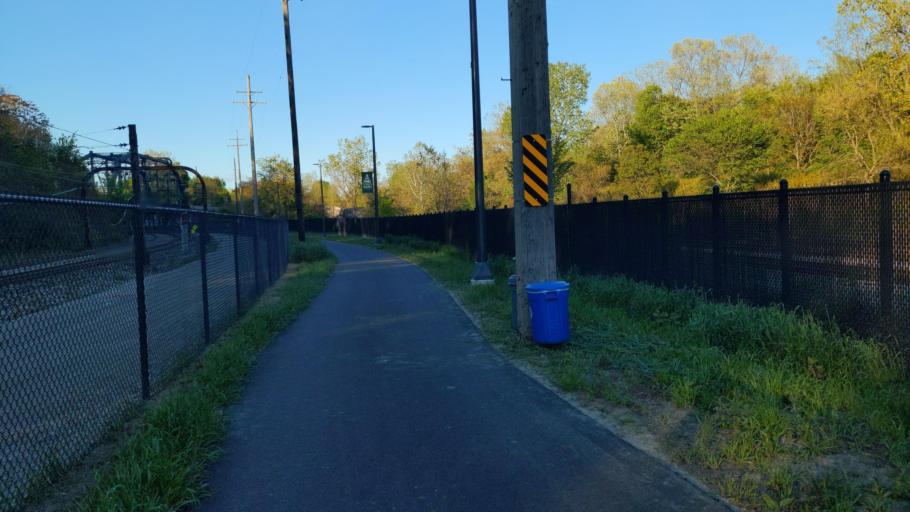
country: US
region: Ohio
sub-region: Cuyahoga County
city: Cleveland
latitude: 41.4762
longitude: -81.7061
